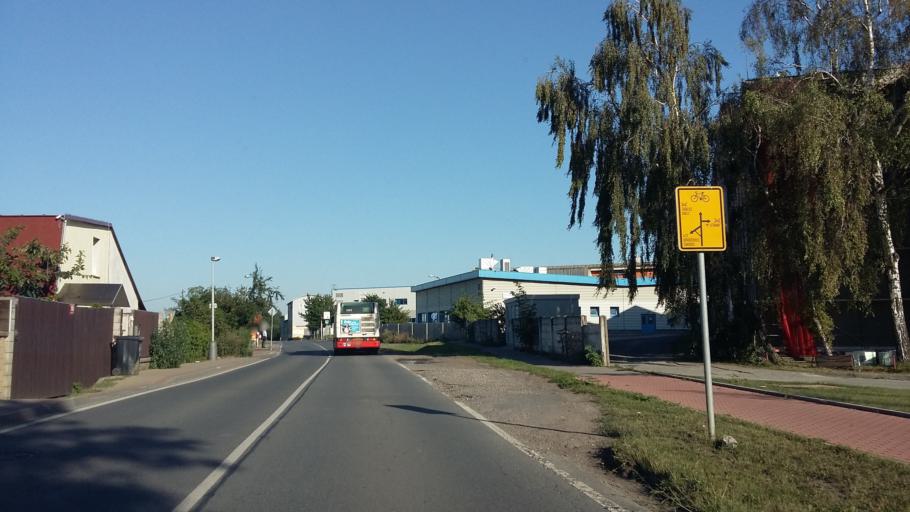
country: CZ
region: Praha
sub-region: Praha 18
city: Letnany
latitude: 50.1364
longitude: 14.5214
